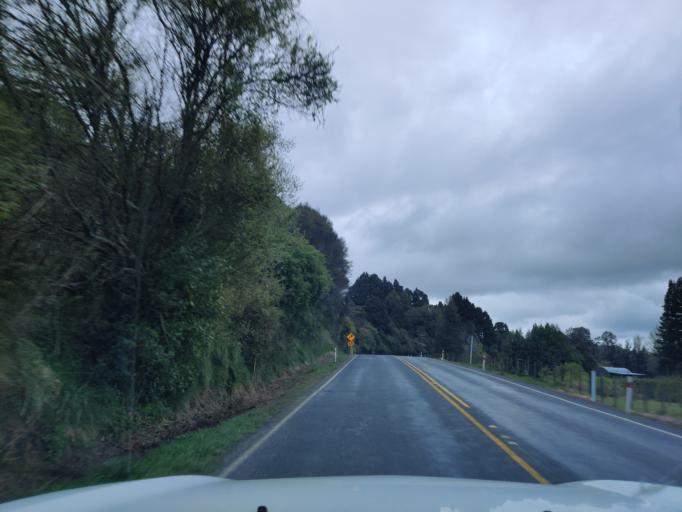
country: NZ
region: Waikato
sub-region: Otorohanga District
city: Otorohanga
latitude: -38.6109
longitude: 175.2177
